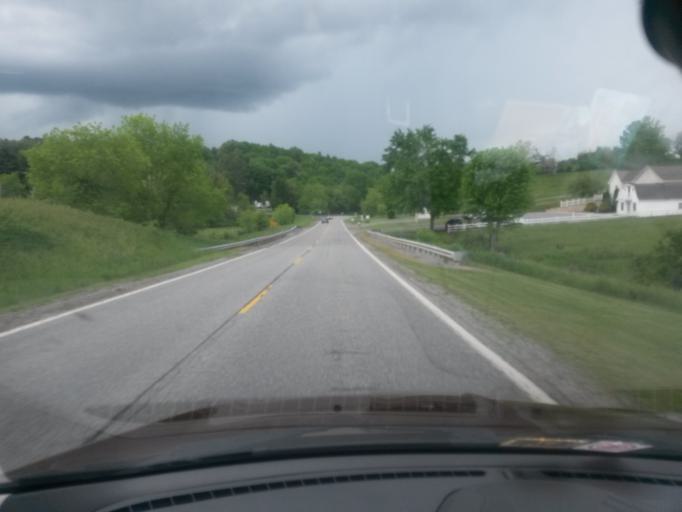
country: US
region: Virginia
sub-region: Floyd County
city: Floyd
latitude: 36.9537
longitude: -80.3641
